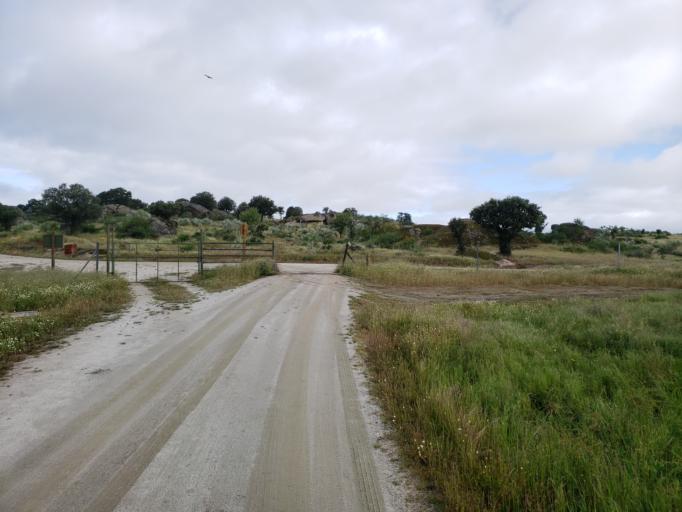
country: ES
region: Extremadura
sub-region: Provincia de Caceres
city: Malpartida de Caceres
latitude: 39.4266
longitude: -6.4935
